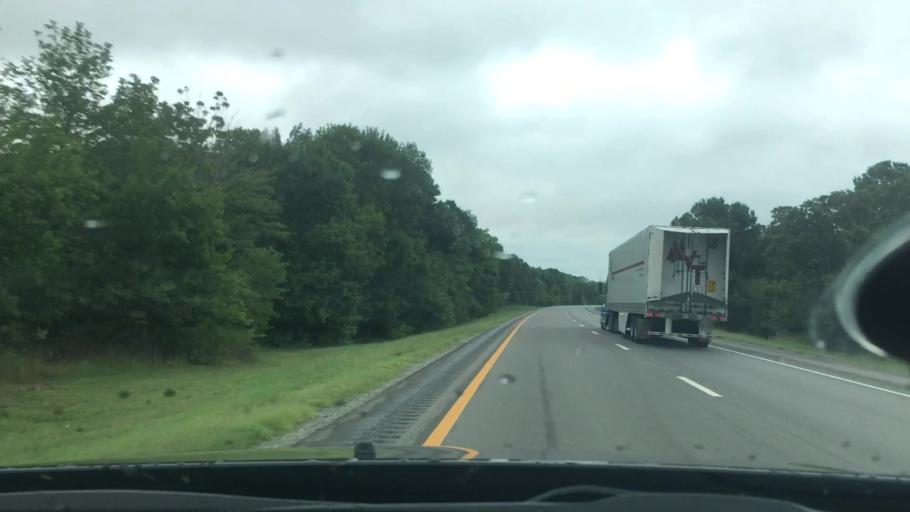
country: US
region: Oklahoma
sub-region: Okmulgee County
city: Morris
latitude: 35.4481
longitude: -95.7607
